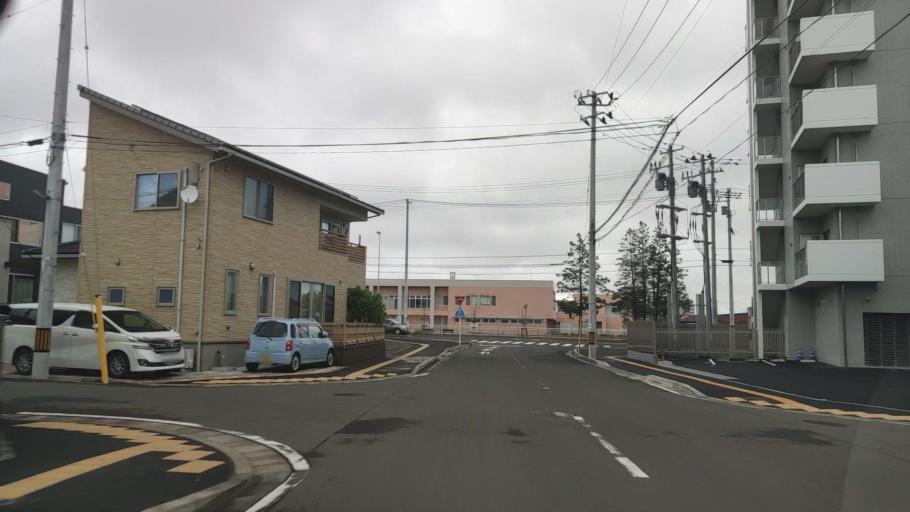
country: JP
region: Miyagi
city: Sendai
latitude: 38.2144
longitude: 140.8726
